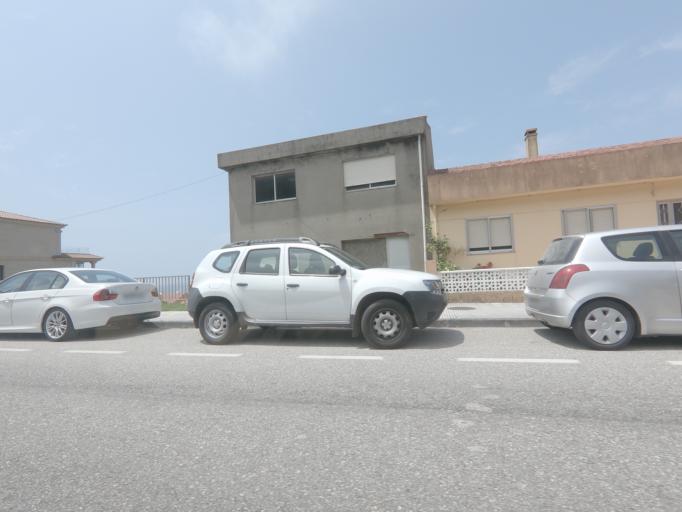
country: ES
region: Galicia
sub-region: Provincia de Pontevedra
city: A Guarda
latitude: 41.8958
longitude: -8.8751
